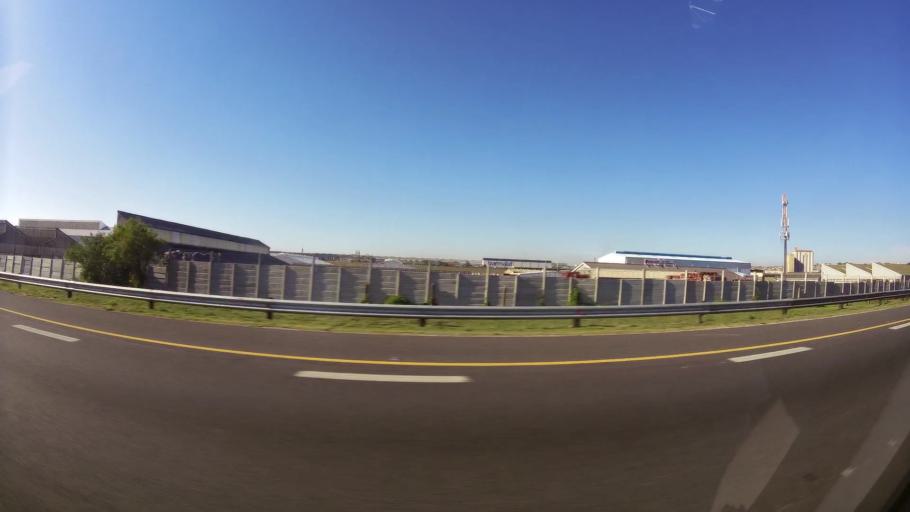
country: ZA
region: Eastern Cape
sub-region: Nelson Mandela Bay Metropolitan Municipality
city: Port Elizabeth
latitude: -33.9166
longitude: 25.5755
